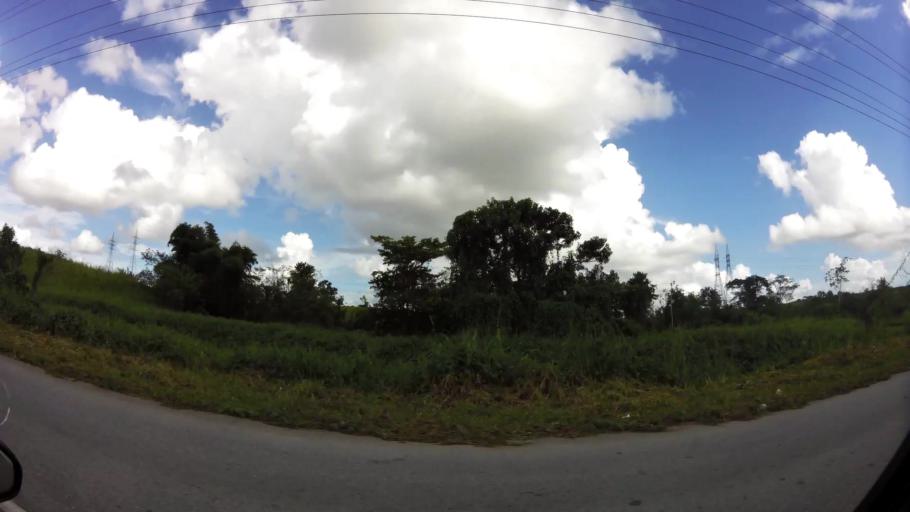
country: TT
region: Penal/Debe
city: Debe
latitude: 10.2347
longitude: -61.4323
